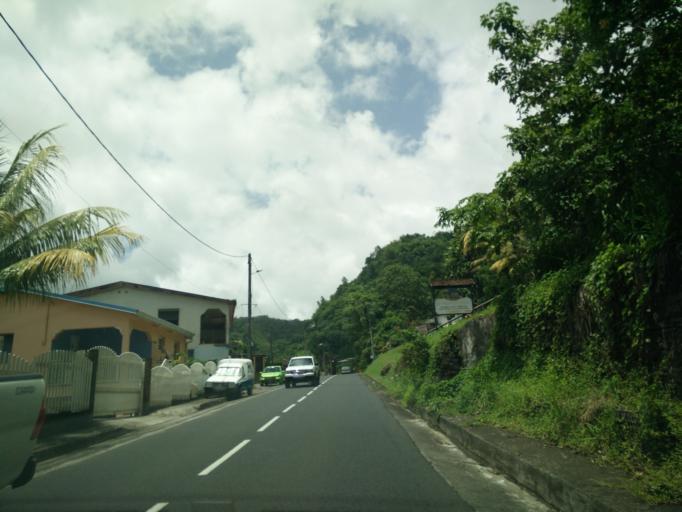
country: MQ
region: Martinique
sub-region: Martinique
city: Saint-Pierre
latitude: 14.7506
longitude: -61.1671
